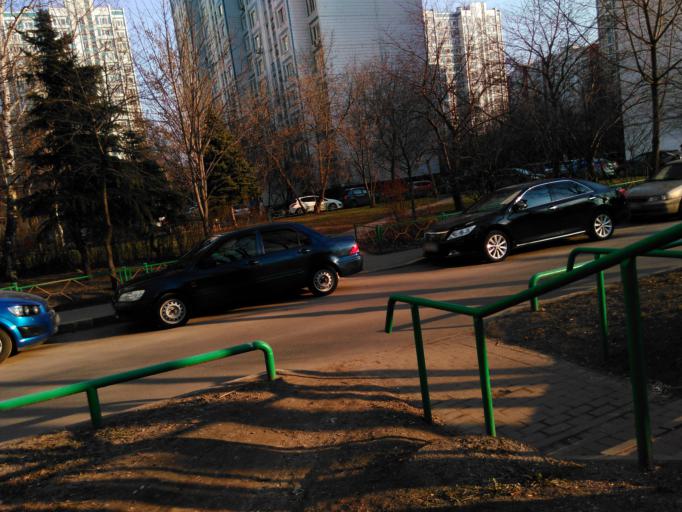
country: RU
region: Moscow
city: Ramenki
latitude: 55.6918
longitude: 37.4947
